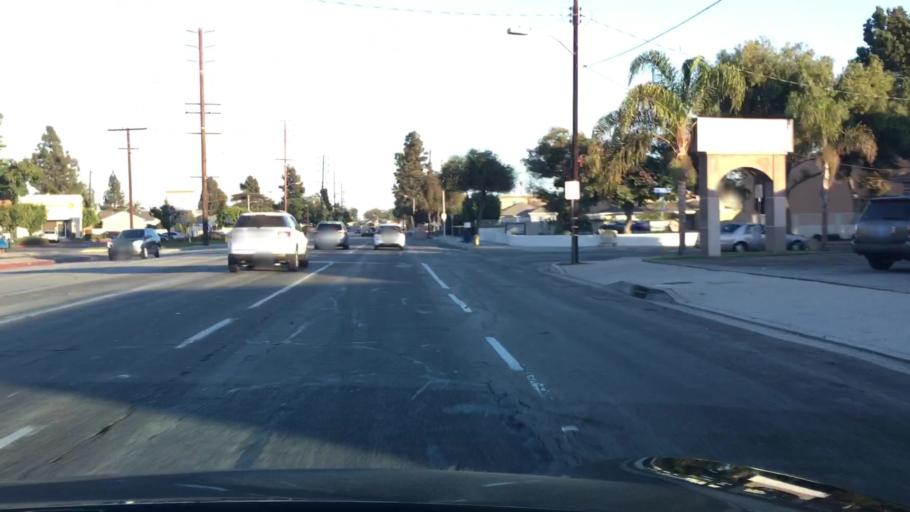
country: US
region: California
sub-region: Los Angeles County
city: Santa Fe Springs
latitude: 33.9543
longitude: -118.1005
